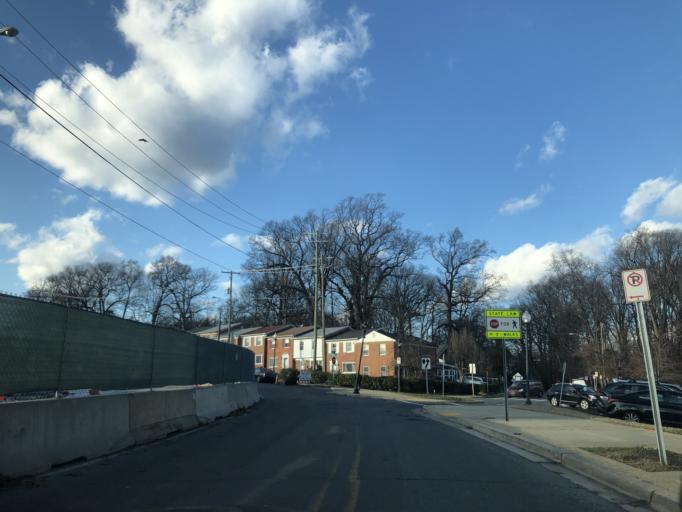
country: US
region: Maryland
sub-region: Montgomery County
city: Takoma Park
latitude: 39.0001
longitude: -77.0015
